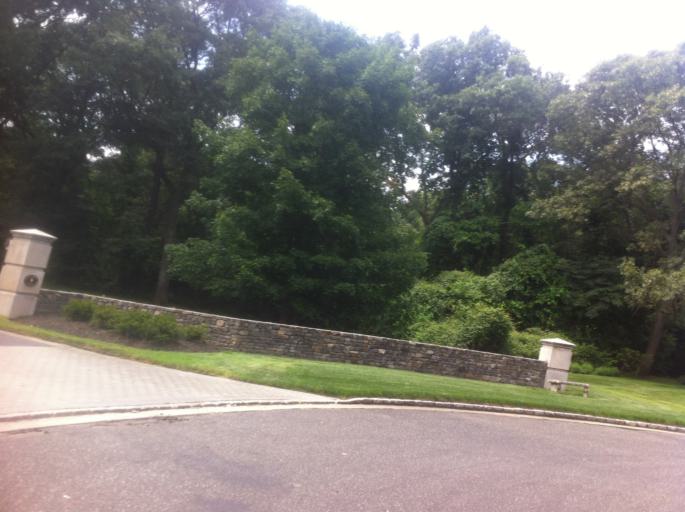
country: US
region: New York
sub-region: Nassau County
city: Upper Brookville
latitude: 40.8431
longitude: -73.5593
